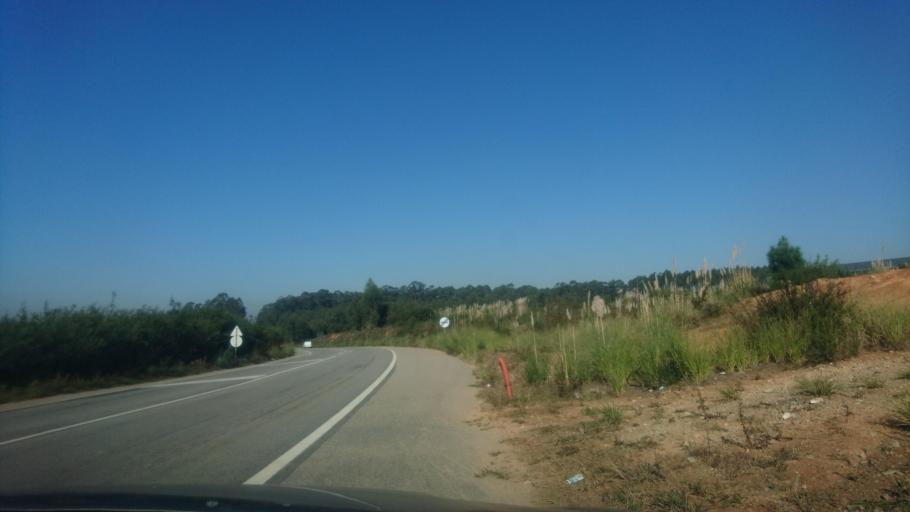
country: PT
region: Aveiro
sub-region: Santa Maria da Feira
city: Rio Meao
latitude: 40.9401
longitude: -8.5817
